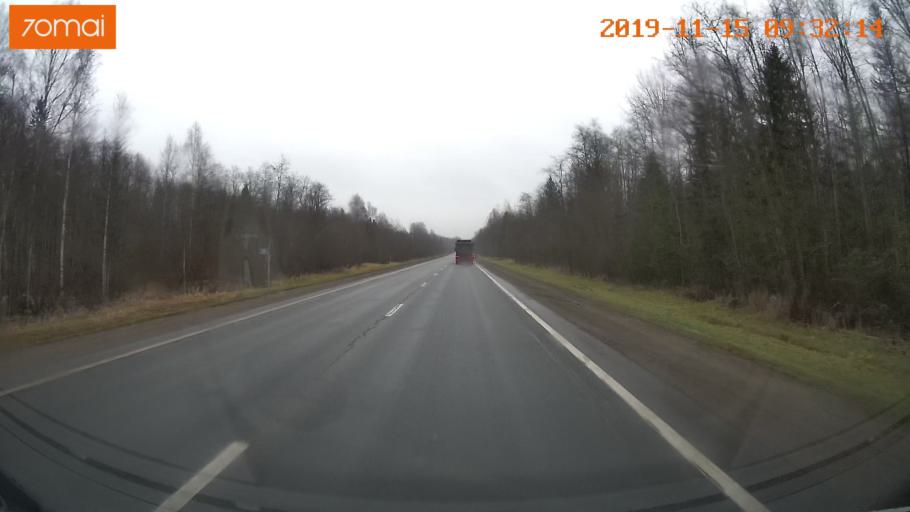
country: RU
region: Vologda
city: Sheksna
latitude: 59.2724
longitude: 38.3299
